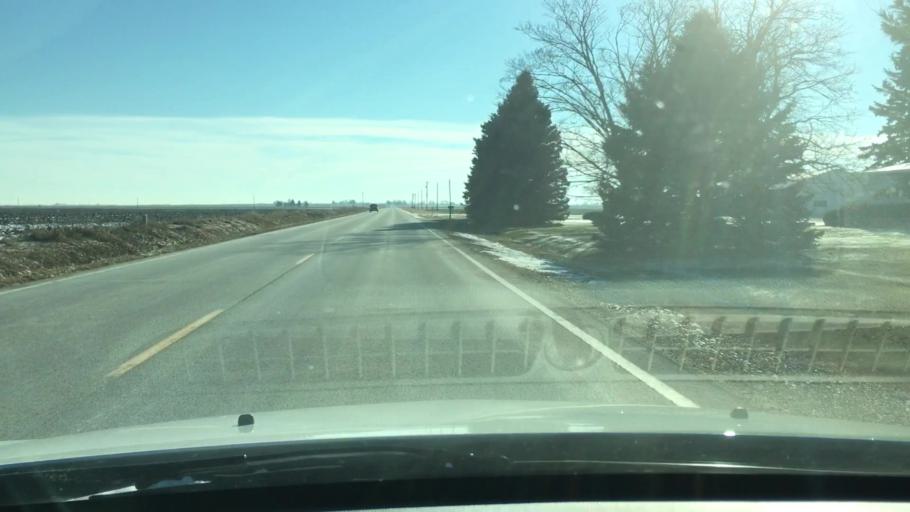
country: US
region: Illinois
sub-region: Ogle County
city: Rochelle
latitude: 41.8657
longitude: -89.0732
